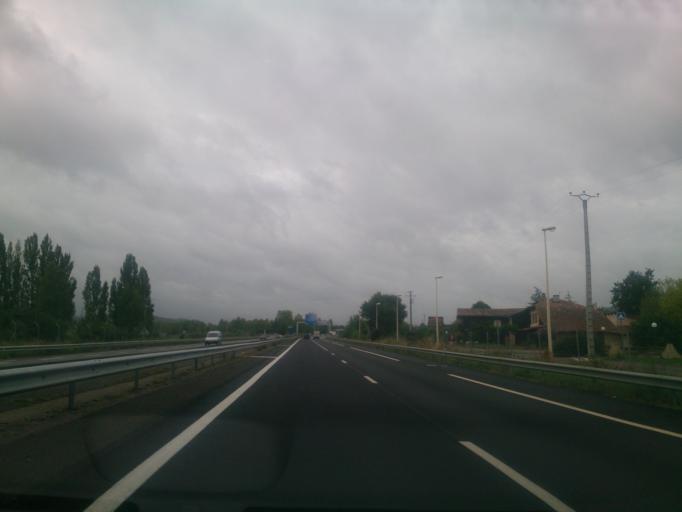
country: FR
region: Midi-Pyrenees
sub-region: Departement de la Haute-Garonne
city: Martres-Tolosane
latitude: 43.2116
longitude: 1.0317
